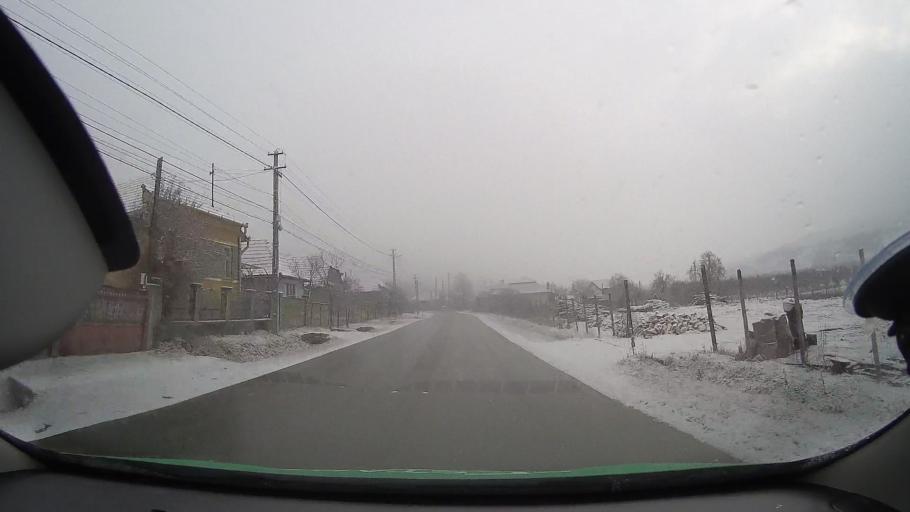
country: RO
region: Alba
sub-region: Municipiul Aiud
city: Ciumbrud
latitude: 46.3113
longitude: 23.7885
